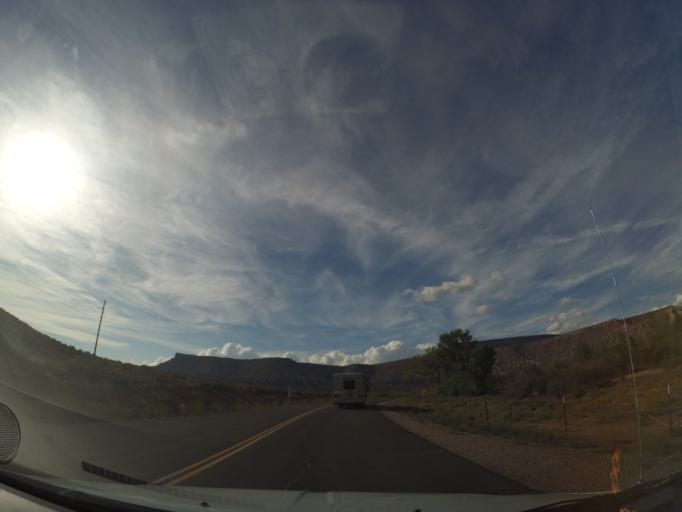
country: US
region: Utah
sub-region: Washington County
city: LaVerkin
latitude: 37.2092
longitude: -113.1753
